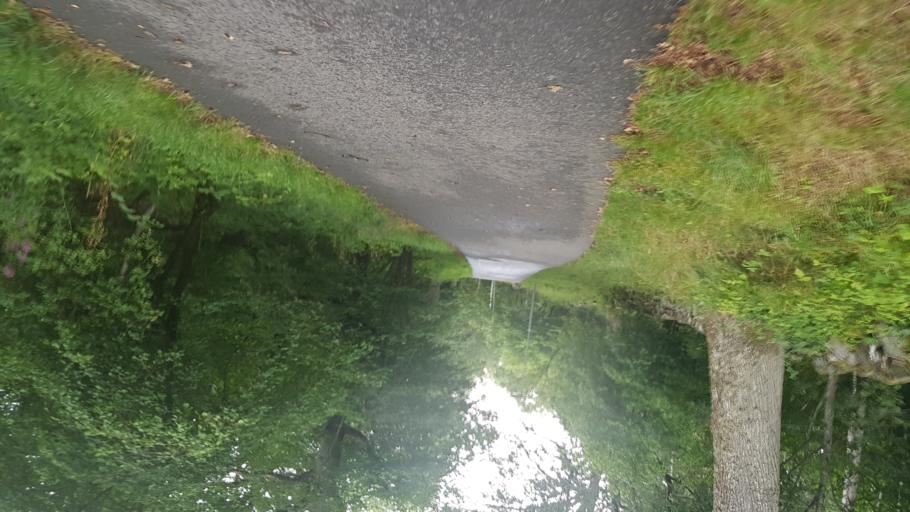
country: SE
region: Vaestra Goetaland
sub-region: Harryda Kommun
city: Molnlycke
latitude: 57.6609
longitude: 12.0997
